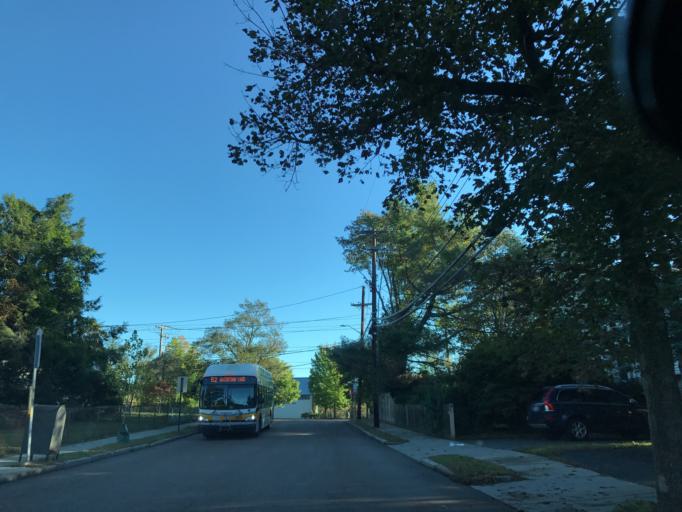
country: US
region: Massachusetts
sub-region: Middlesex County
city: Newton
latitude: 42.2942
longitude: -71.1795
